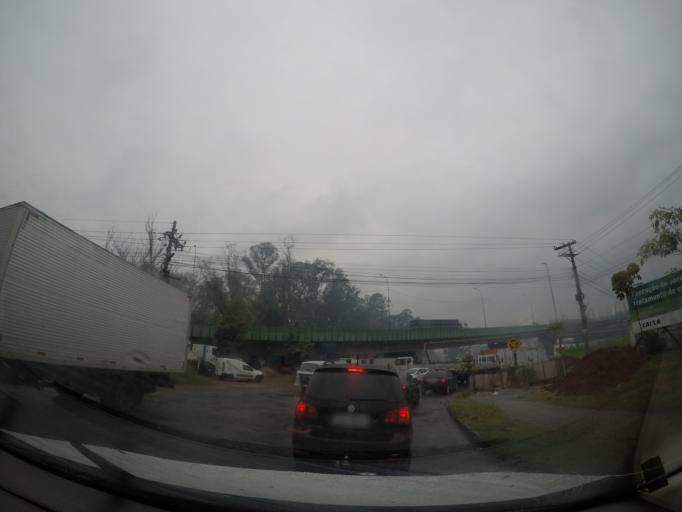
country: BR
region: Sao Paulo
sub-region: Guarulhos
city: Guarulhos
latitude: -23.4788
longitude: -46.4692
